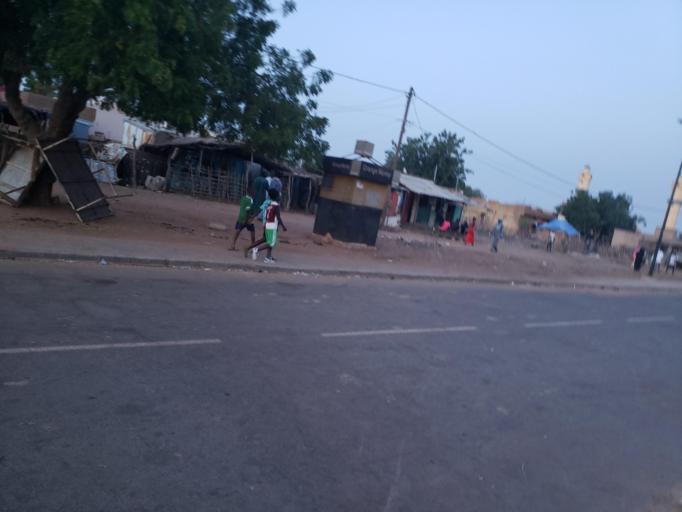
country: SN
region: Matam
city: Ranerou
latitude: 15.2982
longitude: -13.9607
